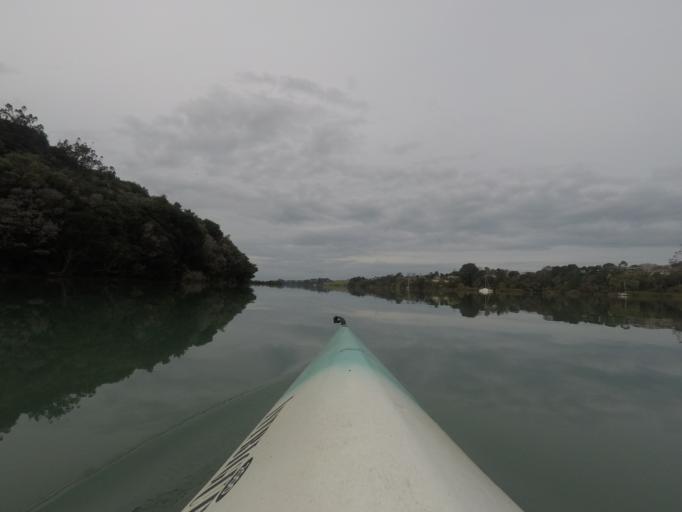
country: NZ
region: Auckland
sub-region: Auckland
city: Rothesay Bay
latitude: -36.6744
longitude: 174.7127
